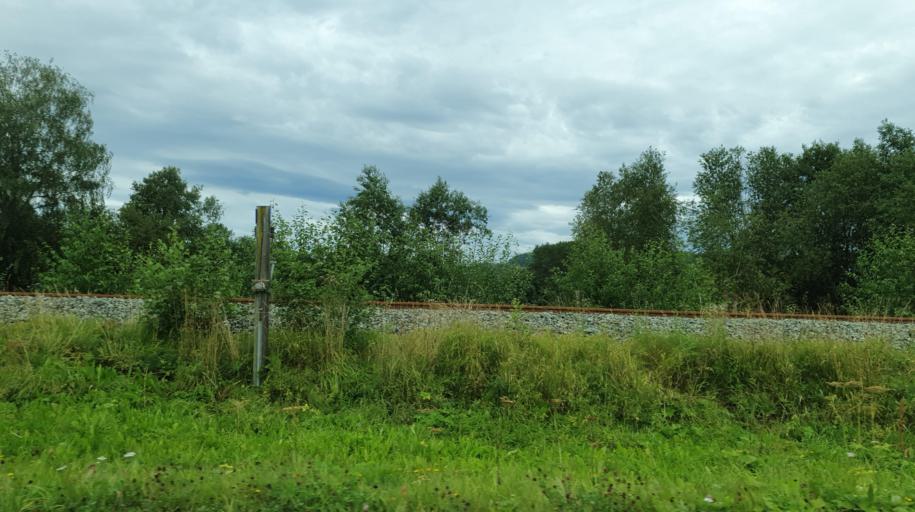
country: NO
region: Nord-Trondelag
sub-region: Stjordal
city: Stjordalshalsen
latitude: 63.4453
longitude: 10.9663
